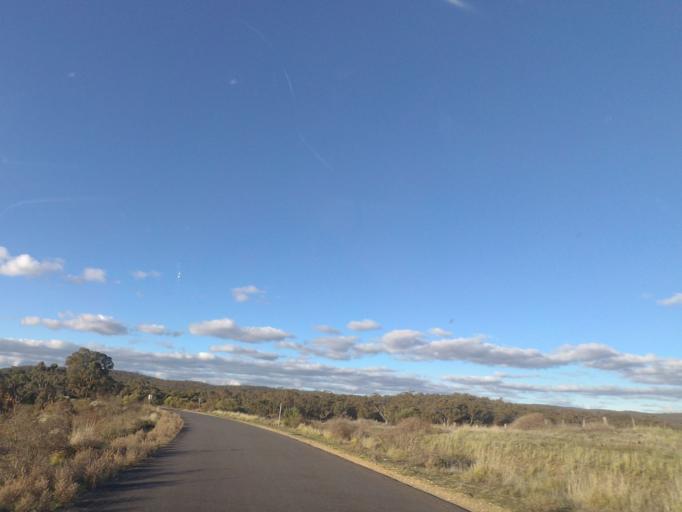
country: AU
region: Victoria
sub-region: Mount Alexander
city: Castlemaine
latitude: -37.1588
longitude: 144.2190
